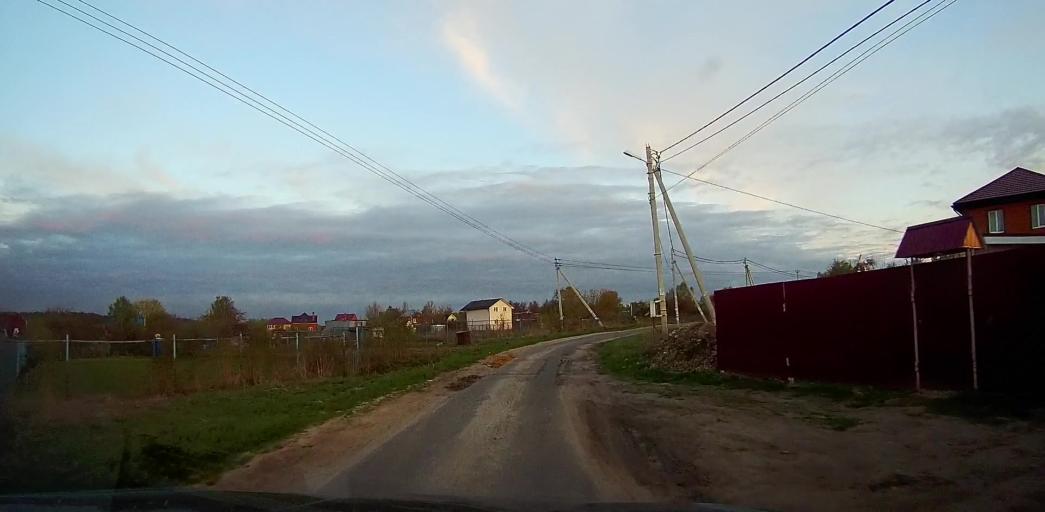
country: RU
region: Moskovskaya
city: Peski
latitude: 55.2109
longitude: 38.7407
